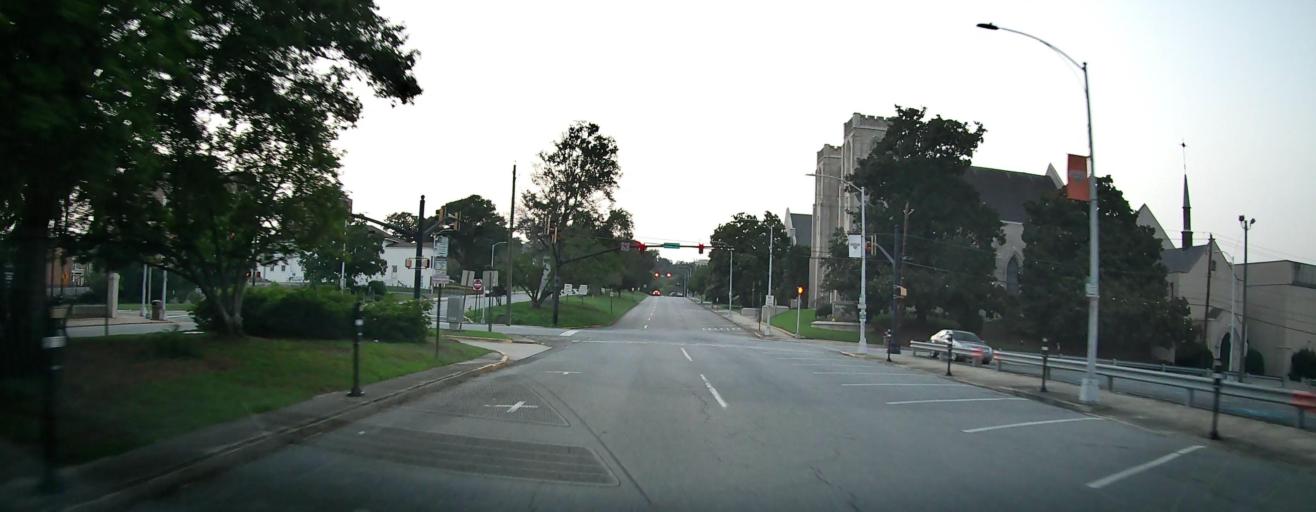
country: US
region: Georgia
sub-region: Bibb County
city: Macon
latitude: 32.8386
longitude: -83.6290
